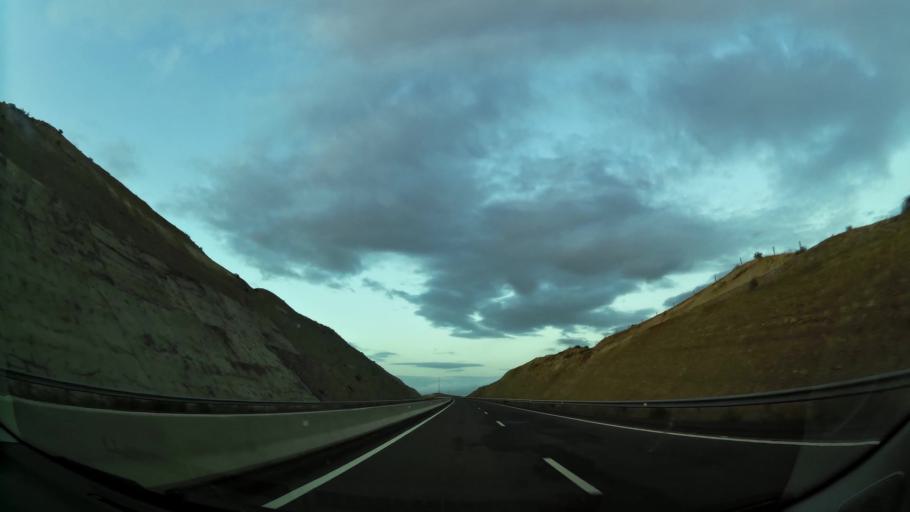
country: MA
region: Oriental
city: El Aioun
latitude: 34.5943
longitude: -2.6639
